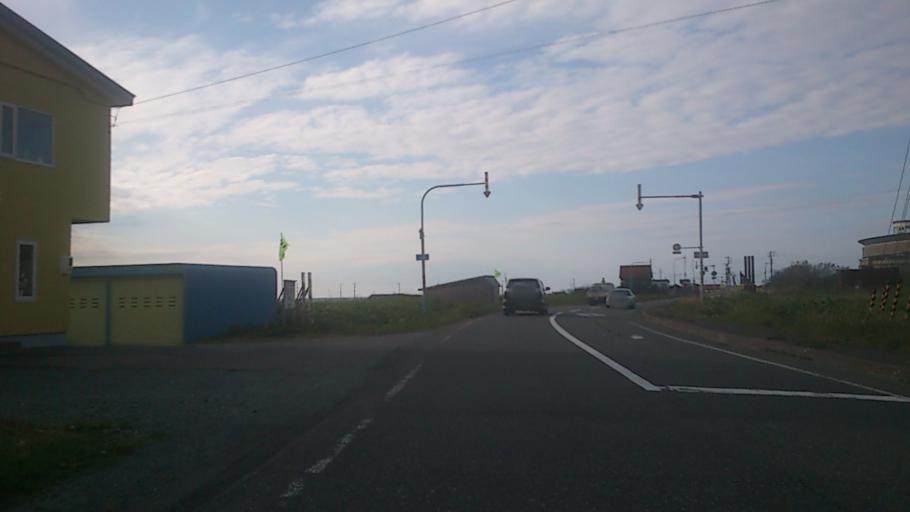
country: JP
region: Hokkaido
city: Wakkanai
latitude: 45.4195
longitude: 141.6373
